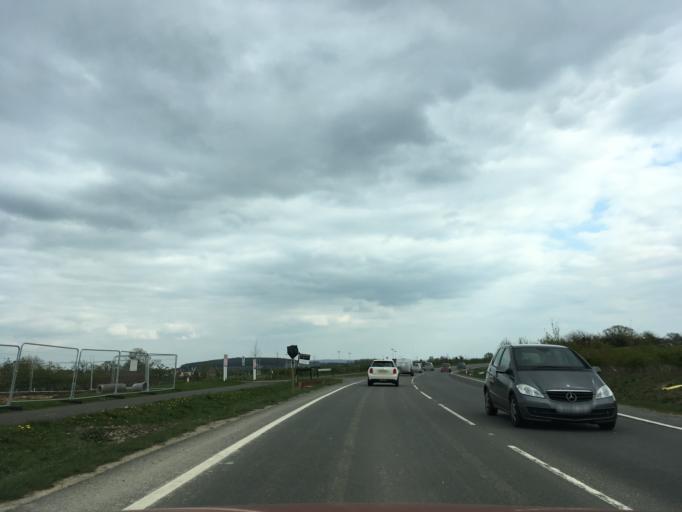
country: GB
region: England
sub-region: Oxfordshire
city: Bicester
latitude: 51.8928
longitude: -1.1785
